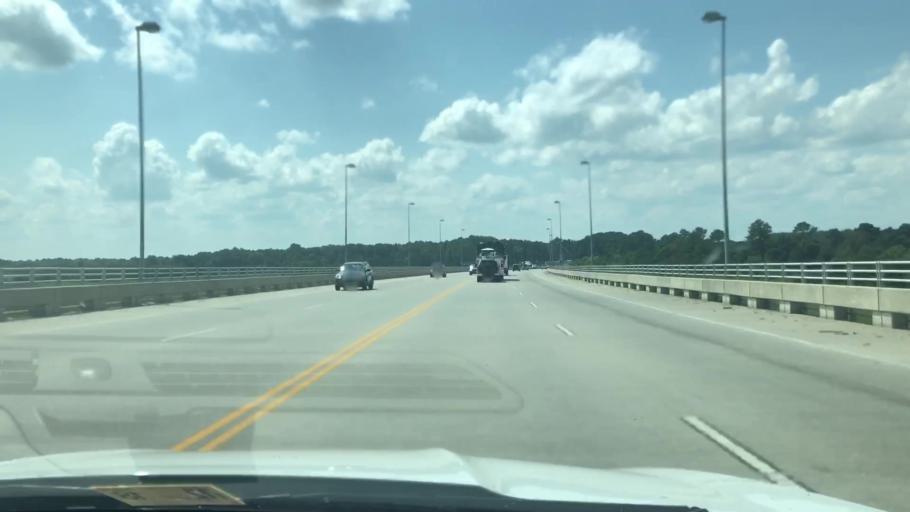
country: US
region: Virginia
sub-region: King William County
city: West Point
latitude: 37.5298
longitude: -76.8136
